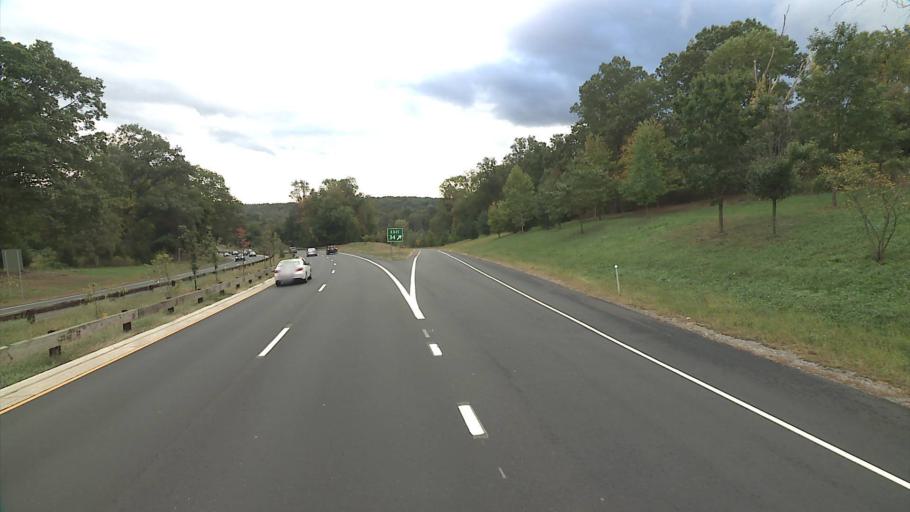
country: US
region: Connecticut
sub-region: Fairfield County
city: North Stamford
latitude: 41.1013
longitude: -73.5704
